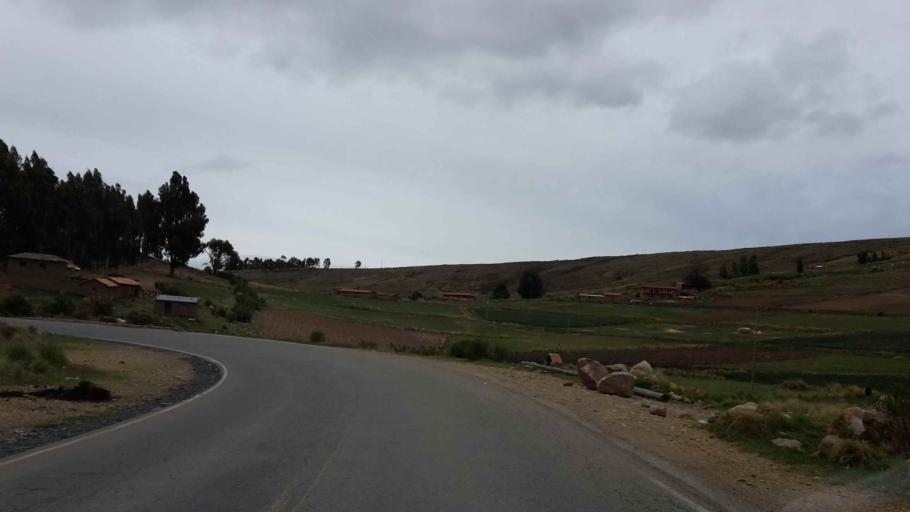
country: BO
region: Cochabamba
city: Arani
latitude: -17.4600
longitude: -65.6765
